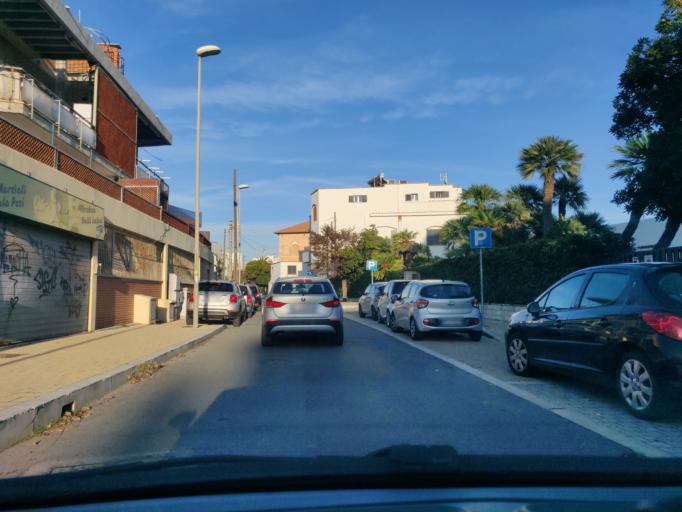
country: IT
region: Latium
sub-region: Citta metropolitana di Roma Capitale
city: Santa Marinella
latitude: 42.0333
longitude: 11.8552
